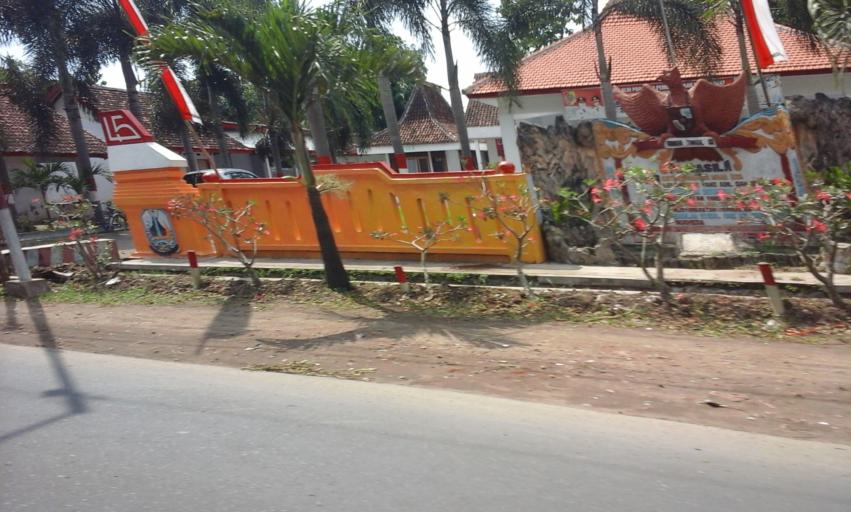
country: ID
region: East Java
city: Krajan Kertonegoro
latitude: -8.3081
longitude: 113.6167
